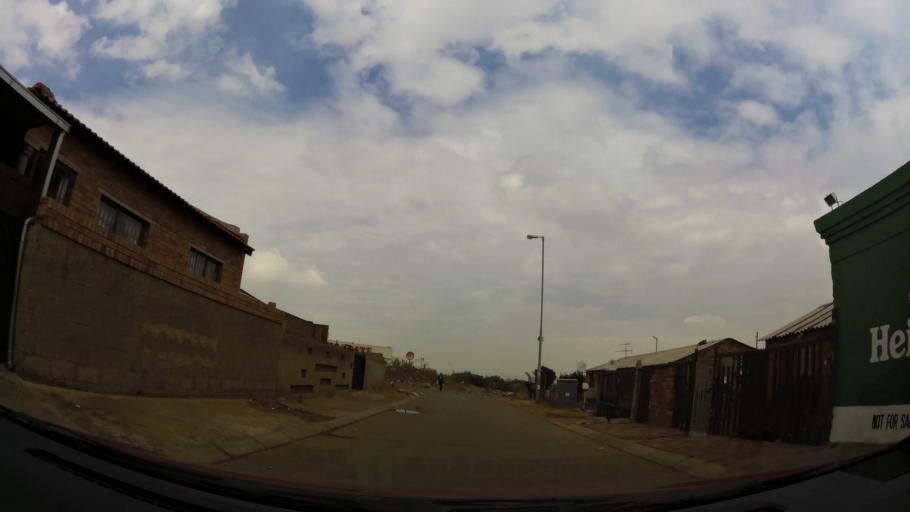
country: ZA
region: Gauteng
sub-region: City of Johannesburg Metropolitan Municipality
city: Soweto
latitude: -26.2545
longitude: 27.8218
